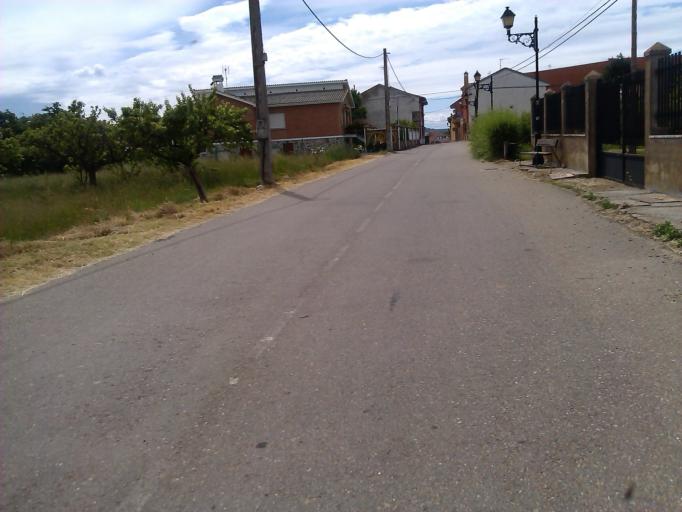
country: ES
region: Castille and Leon
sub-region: Provincia de Leon
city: Hospital de Orbigo
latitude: 42.4640
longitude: -5.8752
